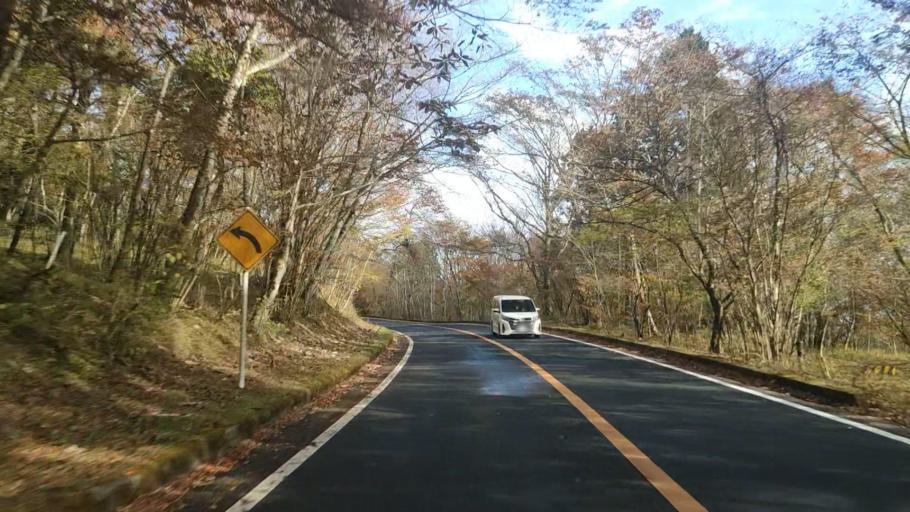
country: JP
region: Shizuoka
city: Fujinomiya
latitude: 35.2947
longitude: 138.7131
